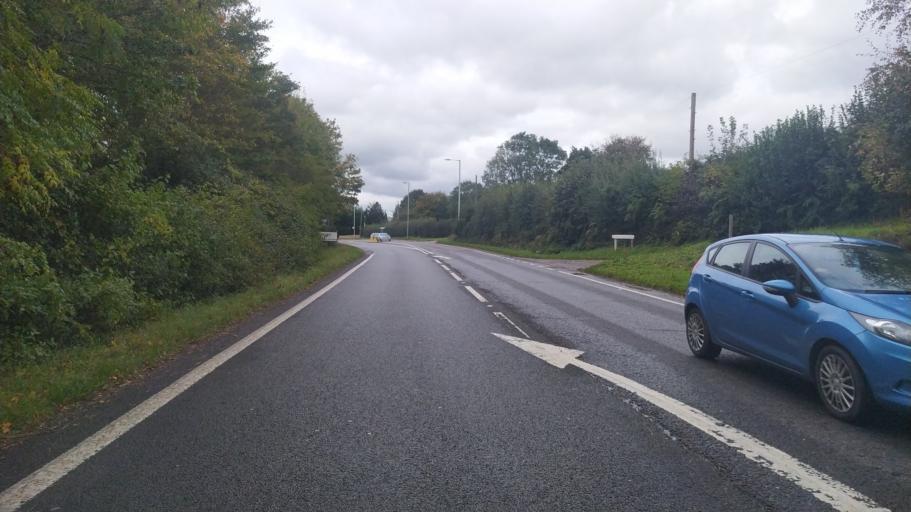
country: GB
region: England
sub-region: Dorset
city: Bridport
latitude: 50.7360
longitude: -2.7361
